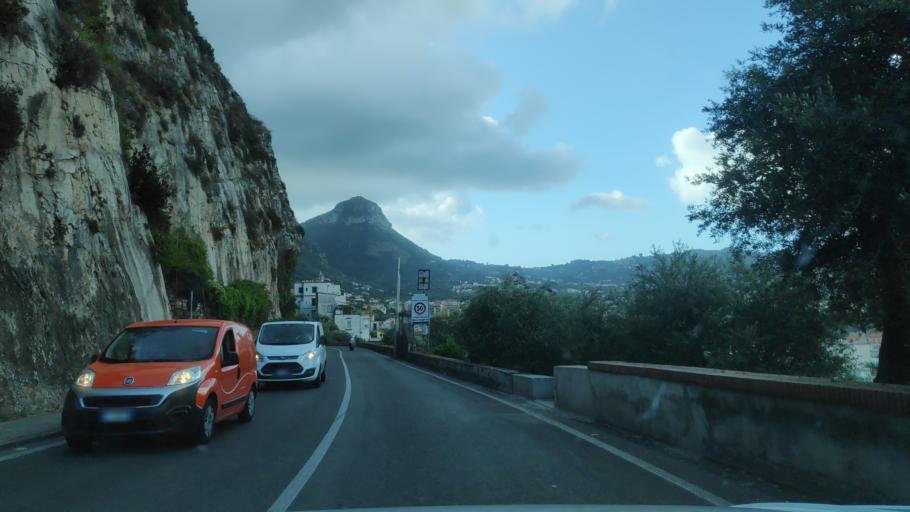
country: IT
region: Campania
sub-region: Provincia di Napoli
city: Meta
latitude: 40.6459
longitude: 14.4136
